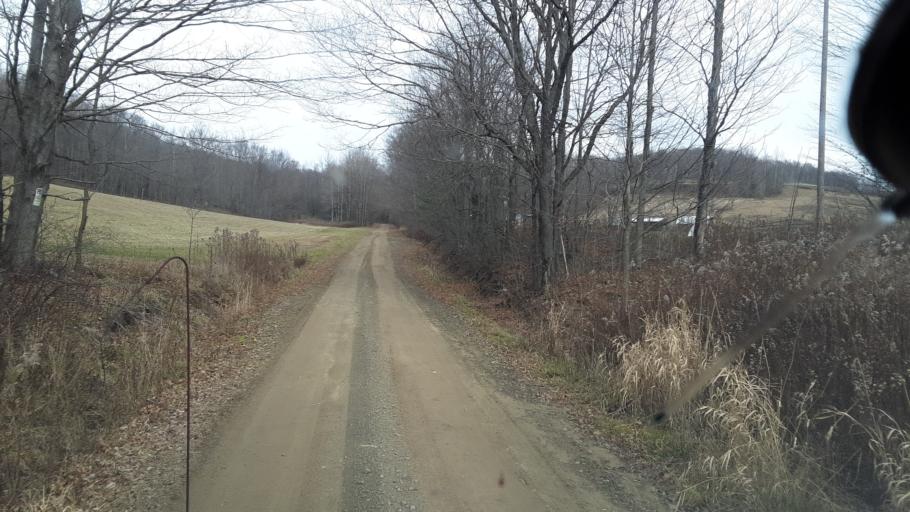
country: US
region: Pennsylvania
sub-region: Tioga County
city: Westfield
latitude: 41.9152
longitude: -77.7058
